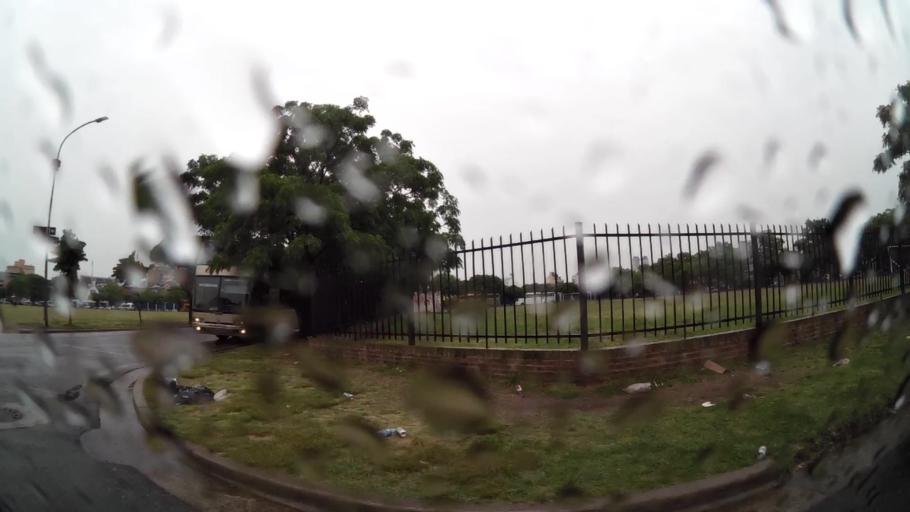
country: AR
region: Buenos Aires F.D.
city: Buenos Aires
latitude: -34.6313
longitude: -58.3645
